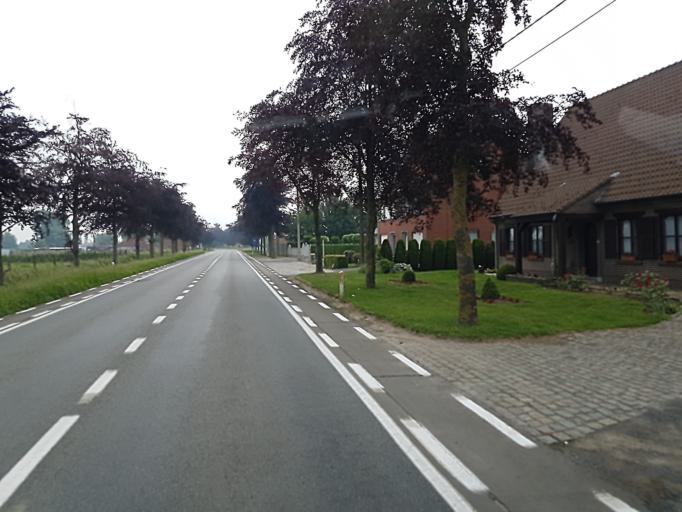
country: BE
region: Flanders
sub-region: Provincie West-Vlaanderen
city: Dentergem
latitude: 50.9562
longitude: 3.3715
